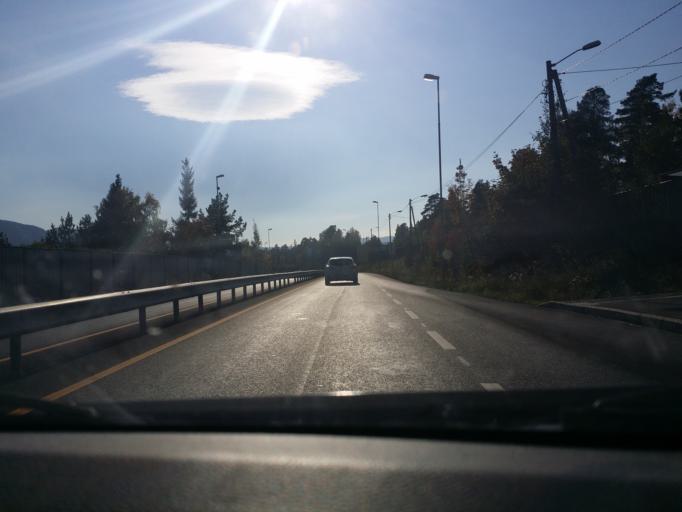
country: NO
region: Buskerud
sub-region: Hole
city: Vik
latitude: 60.0881
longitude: 10.2874
